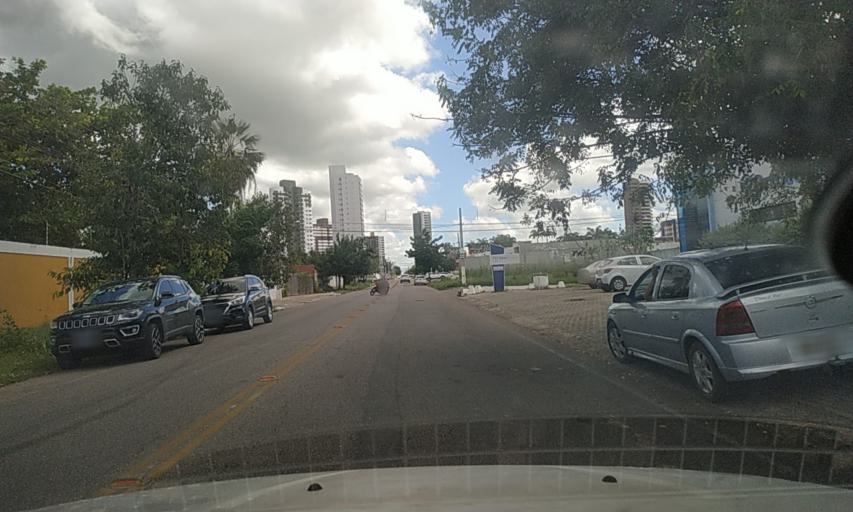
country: BR
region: Rio Grande do Norte
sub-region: Mossoro
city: Mossoro
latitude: -5.1824
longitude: -37.3564
